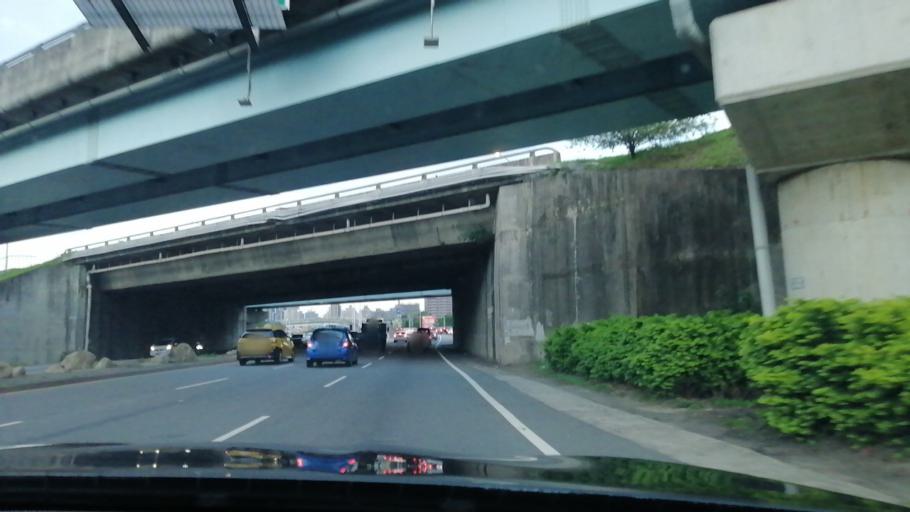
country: TW
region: Taiwan
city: Taoyuan City
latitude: 24.9984
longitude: 121.2830
